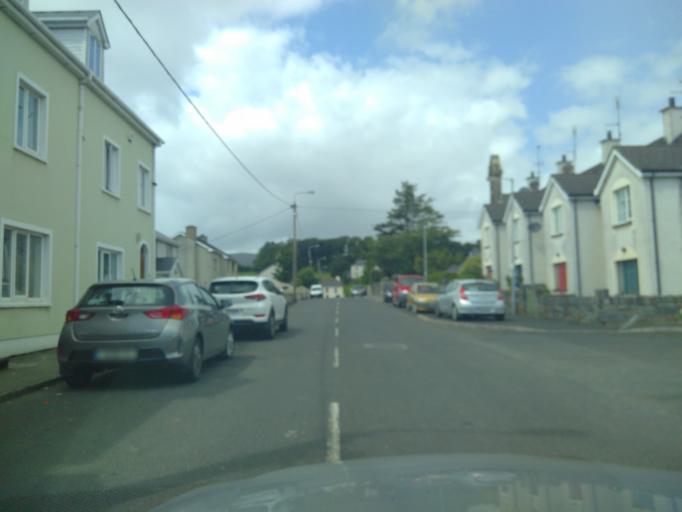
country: IE
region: Ulster
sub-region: County Donegal
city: Buncrana
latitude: 55.0956
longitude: -7.5343
